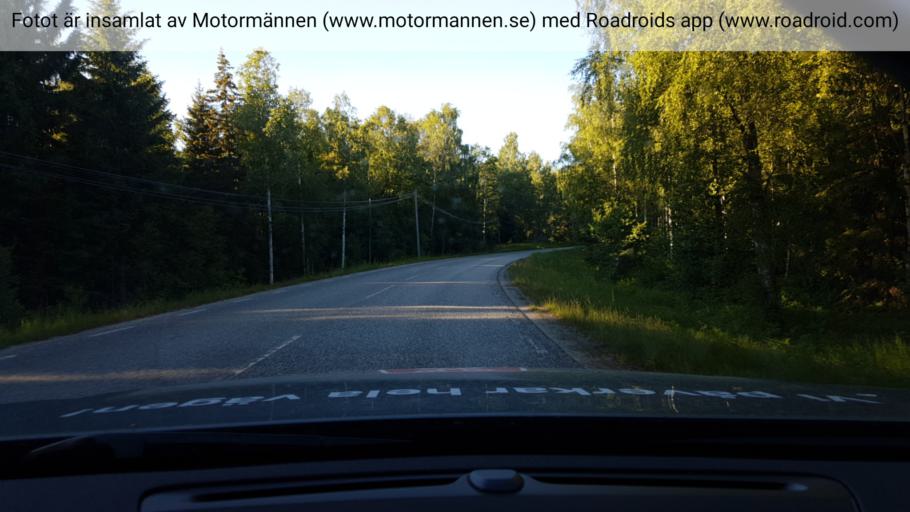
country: SE
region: Stockholm
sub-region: Haninge Kommun
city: Jordbro
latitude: 58.9932
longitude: 18.1007
